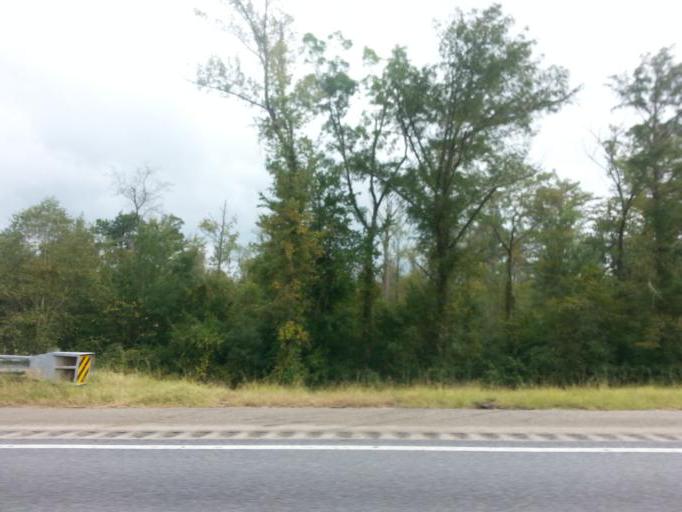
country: US
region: Alabama
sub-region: Escambia County
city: Brewton
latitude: 31.3055
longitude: -87.1660
